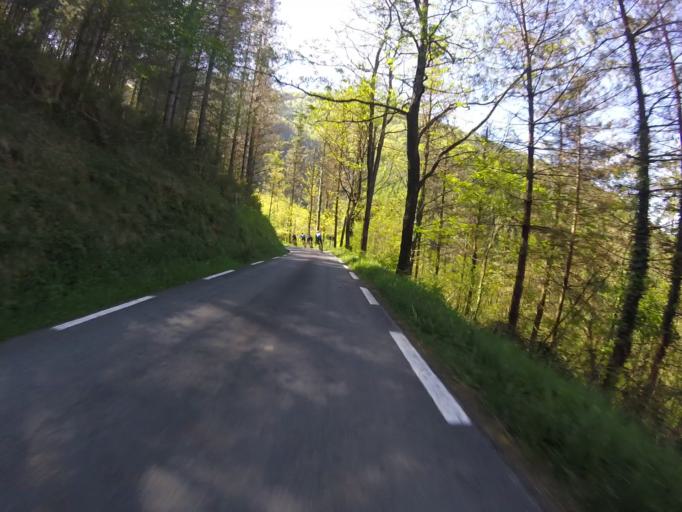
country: ES
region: Basque Country
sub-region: Provincia de Guipuzcoa
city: Errezil
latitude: 43.1888
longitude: -2.1900
